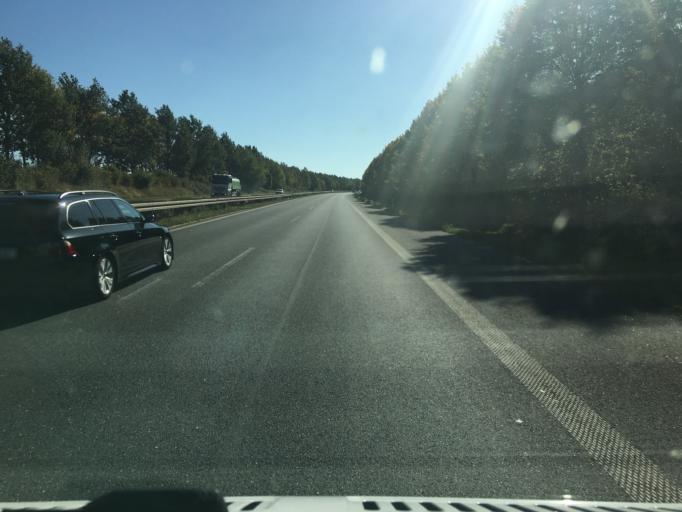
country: DE
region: Saxony
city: Dennheritz
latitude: 50.8104
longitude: 12.4521
